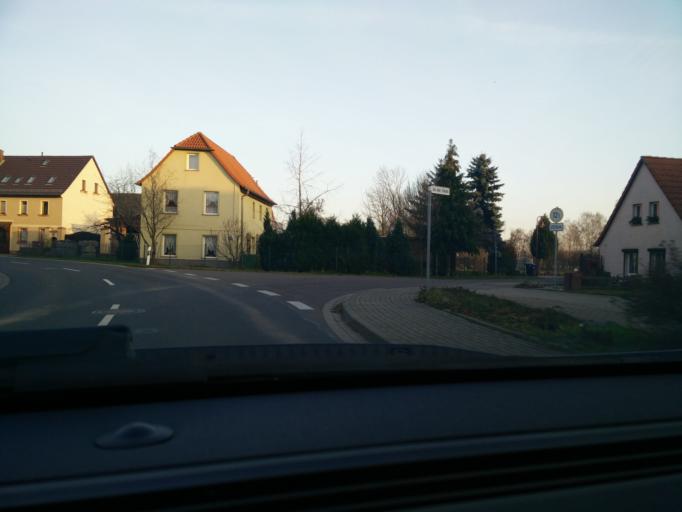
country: DE
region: Saxony
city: Espenhain
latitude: 51.2089
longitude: 12.4829
